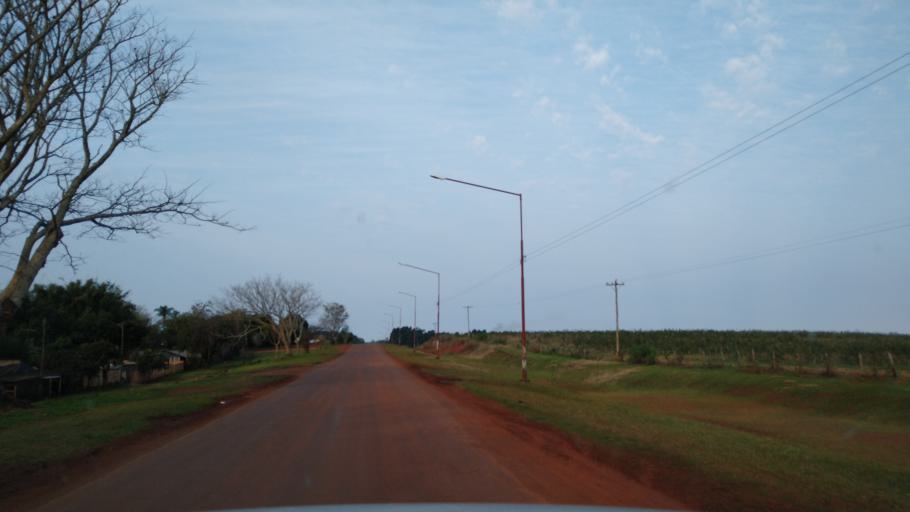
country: AR
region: Corrientes
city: San Carlos
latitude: -27.7520
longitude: -55.8975
